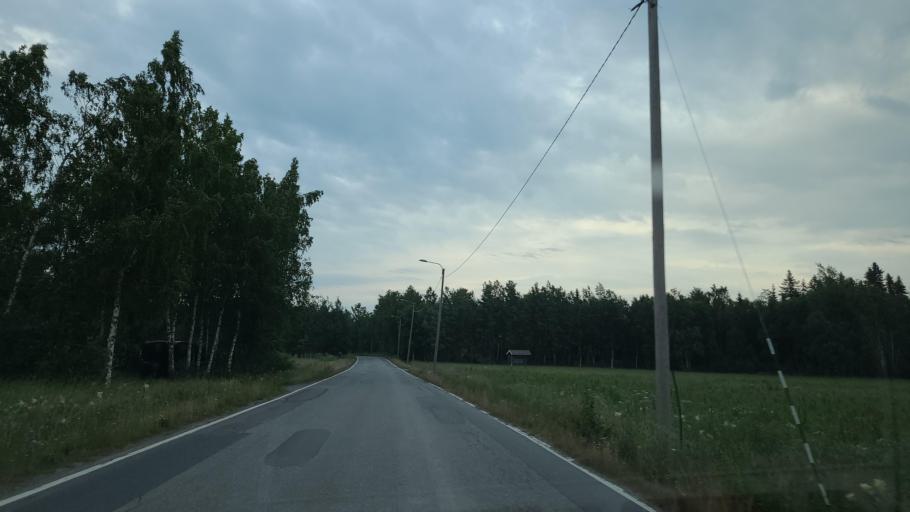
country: FI
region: Ostrobothnia
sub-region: Vaasa
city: Replot
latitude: 63.1867
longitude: 21.2986
